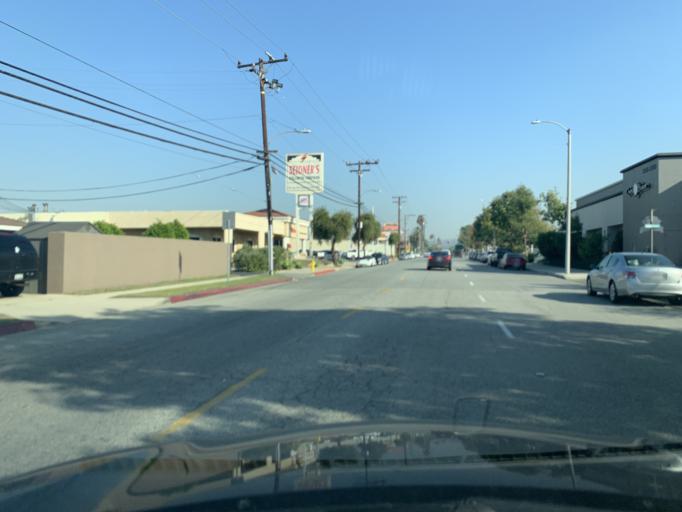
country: US
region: California
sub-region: Los Angeles County
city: Covina
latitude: 34.0754
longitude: -117.8926
